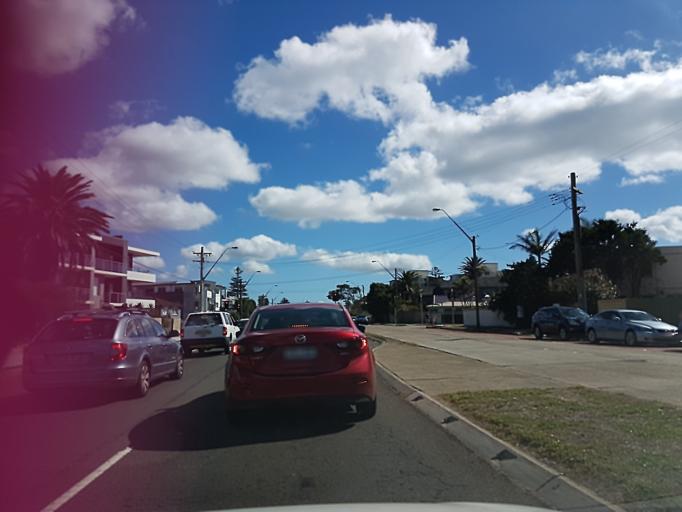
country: AU
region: New South Wales
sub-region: Warringah
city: Narrabeen
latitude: -33.7229
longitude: 151.2986
